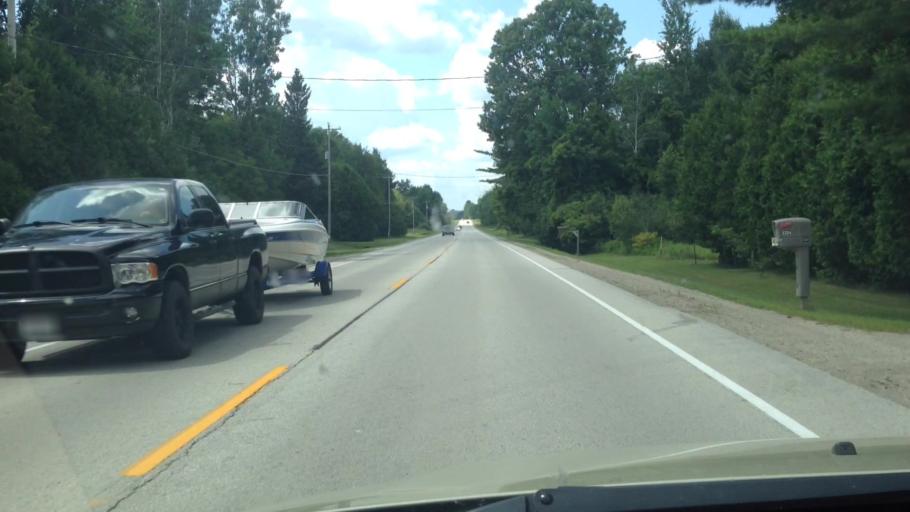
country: US
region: Wisconsin
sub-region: Brown County
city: Suamico
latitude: 44.6395
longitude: -88.0735
